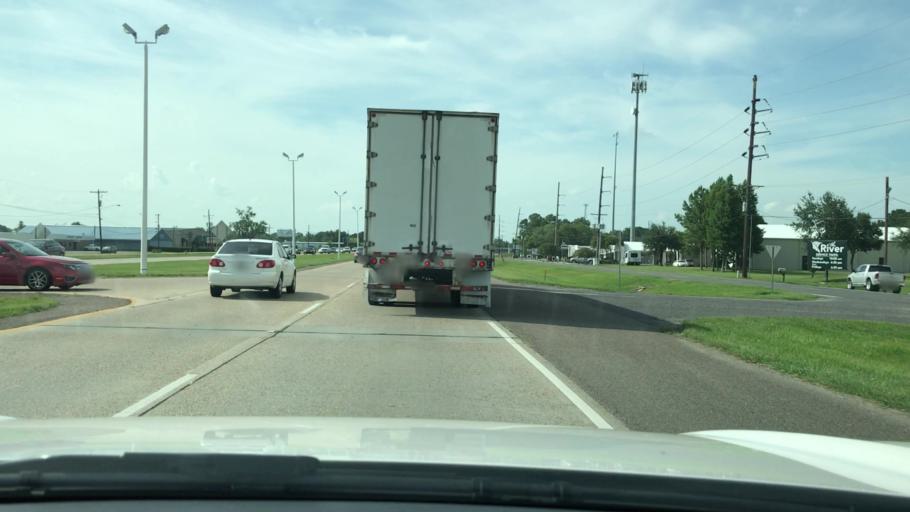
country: US
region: Louisiana
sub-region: West Baton Rouge Parish
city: Addis
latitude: 30.3575
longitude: -91.2599
